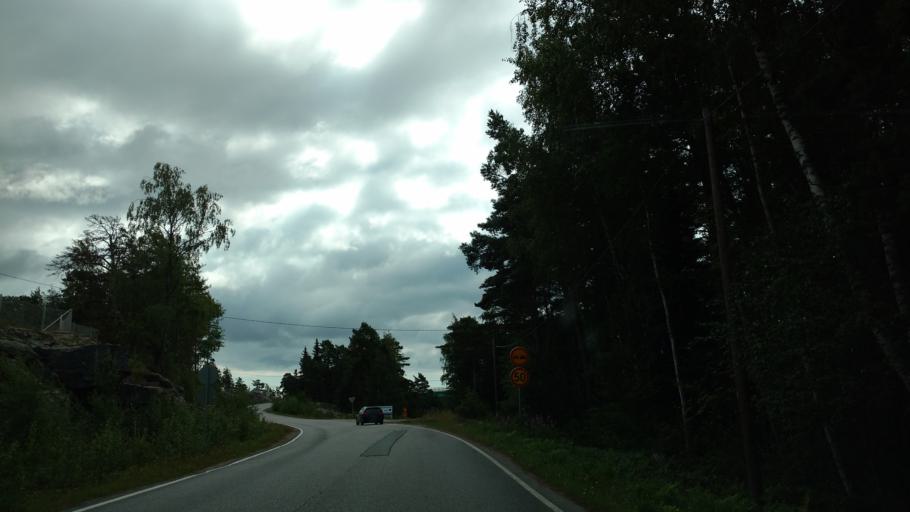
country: FI
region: Varsinais-Suomi
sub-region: Aboland-Turunmaa
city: Dragsfjaerd
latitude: 59.9886
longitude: 22.4521
